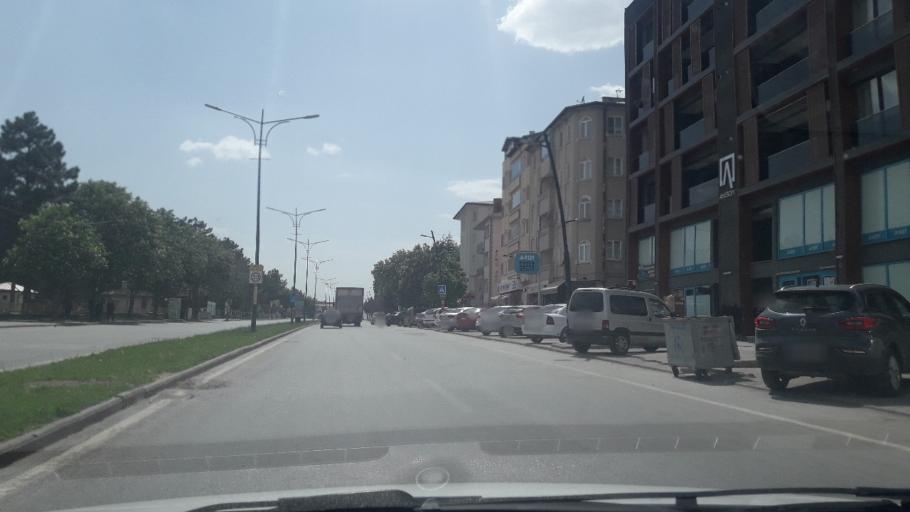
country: TR
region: Sivas
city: Sivas
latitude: 39.7345
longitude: 36.9916
